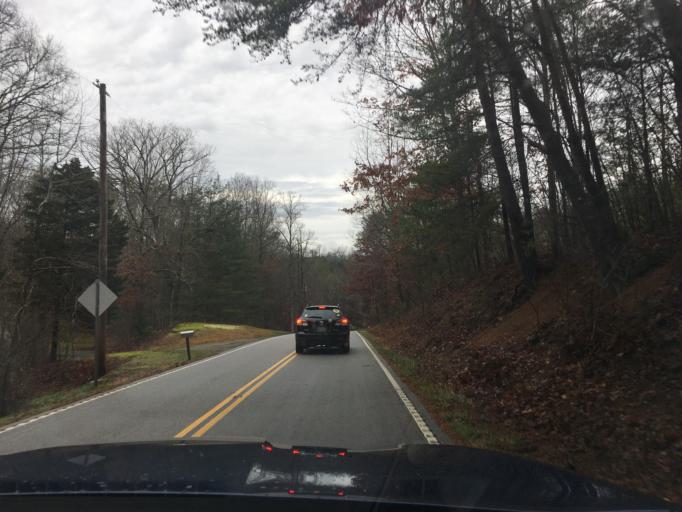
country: US
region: Tennessee
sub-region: McMinn County
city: Englewood
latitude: 35.3514
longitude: -84.4039
